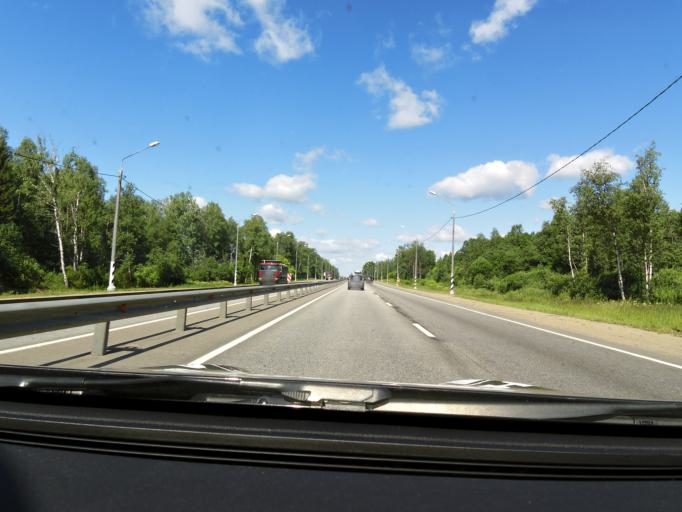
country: RU
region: Tverskaya
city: Likhoslavl'
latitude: 56.9527
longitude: 35.3931
